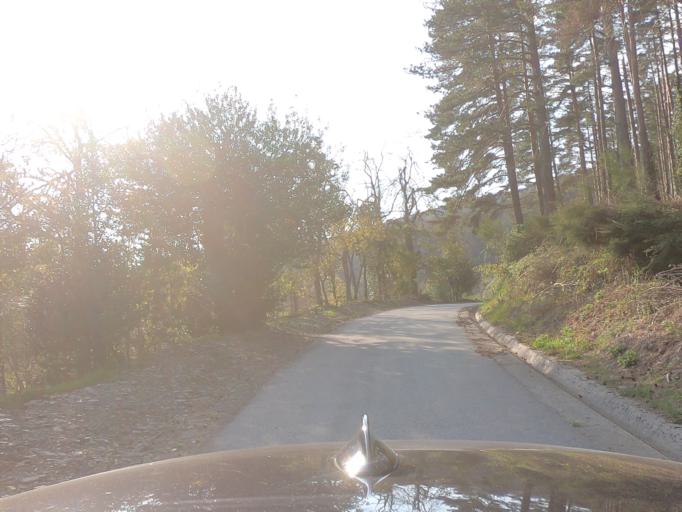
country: PT
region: Vila Real
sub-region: Vila Real
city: Vila Real
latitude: 41.3180
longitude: -7.8651
